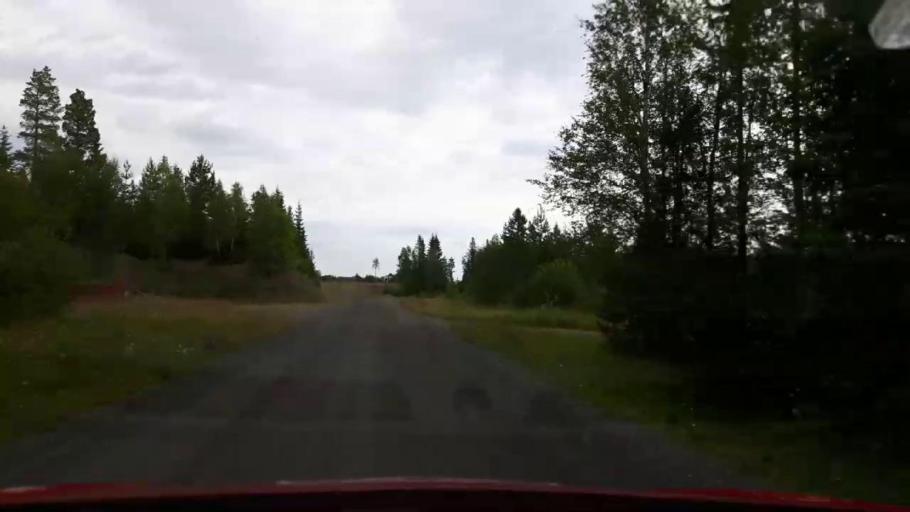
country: SE
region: Jaemtland
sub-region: OEstersunds Kommun
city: Lit
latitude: 63.4092
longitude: 15.2403
